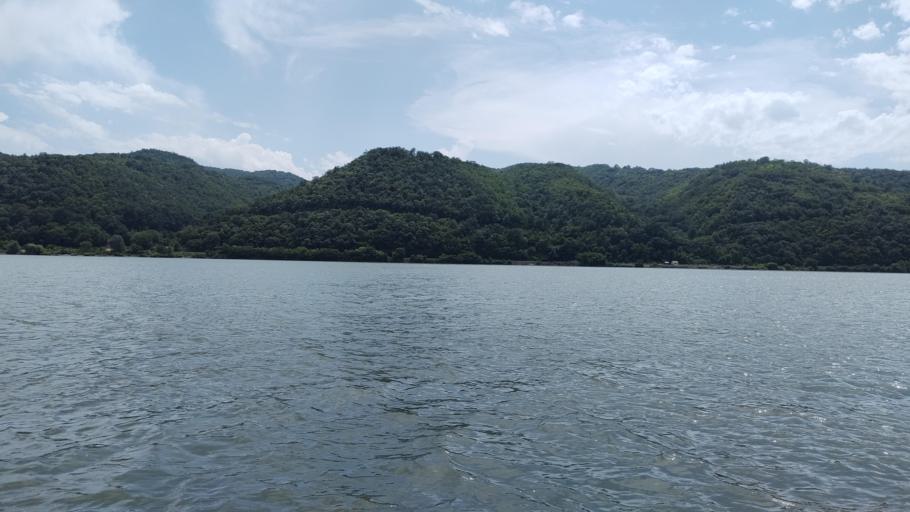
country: RO
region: Caras-Severin
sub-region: Comuna Berzasca
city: Berzasca
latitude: 44.6441
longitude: 21.9275
